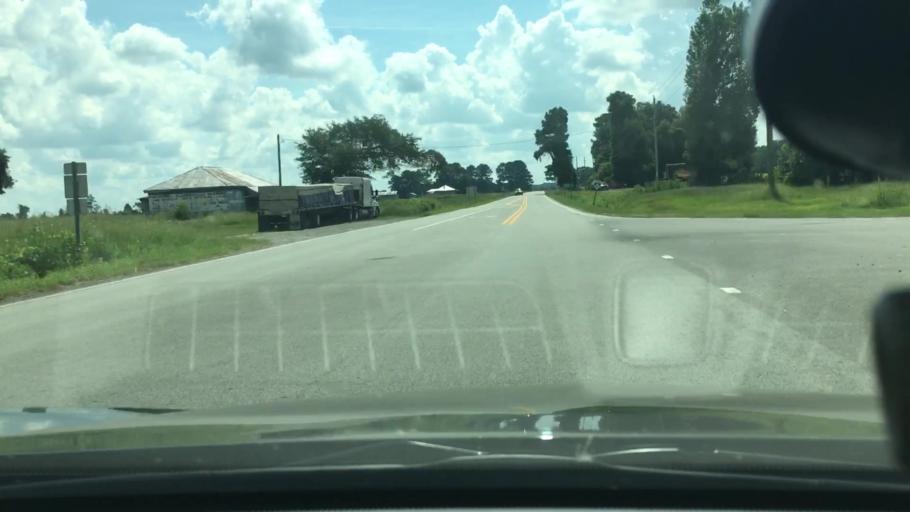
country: US
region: North Carolina
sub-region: Pitt County
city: Farmville
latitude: 35.6733
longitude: -77.4855
